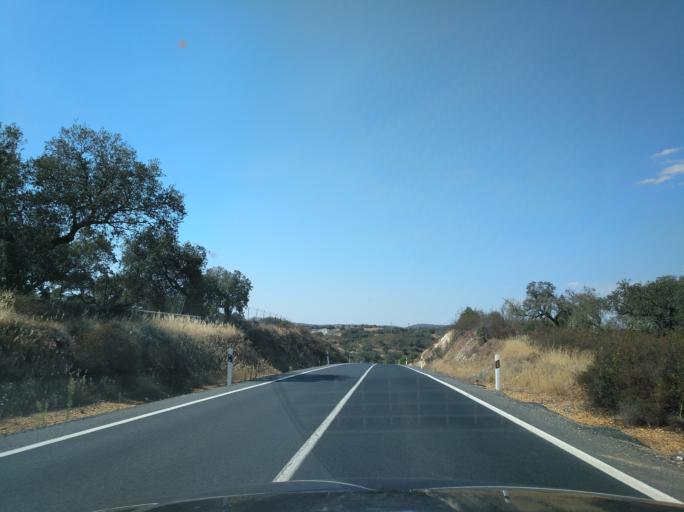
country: ES
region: Andalusia
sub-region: Provincia de Huelva
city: Alosno
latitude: 37.5207
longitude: -7.1347
